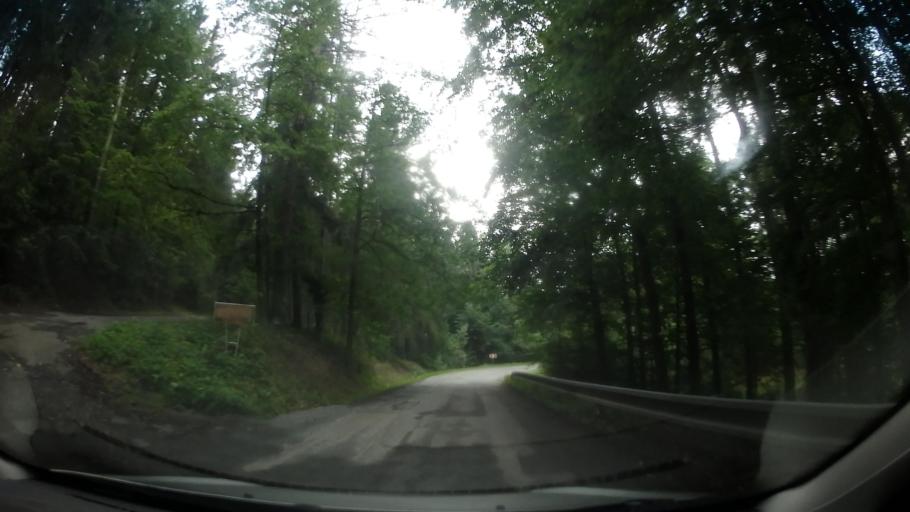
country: CZ
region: Central Bohemia
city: Neveklov
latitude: 49.7271
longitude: 14.4926
